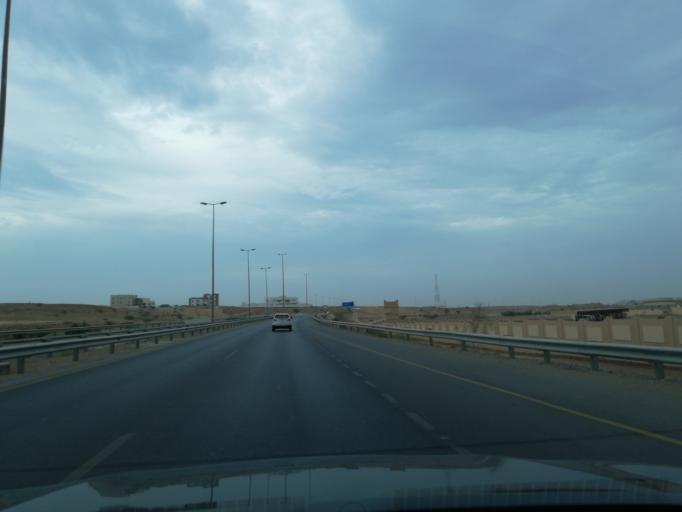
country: OM
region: Muhafazat Masqat
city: Bawshar
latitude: 23.5496
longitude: 58.3665
